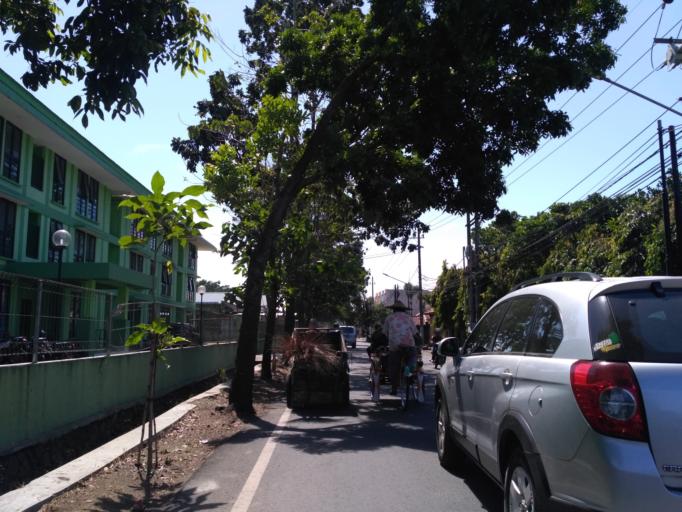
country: ID
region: East Java
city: Malang
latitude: -7.9832
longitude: 112.6473
